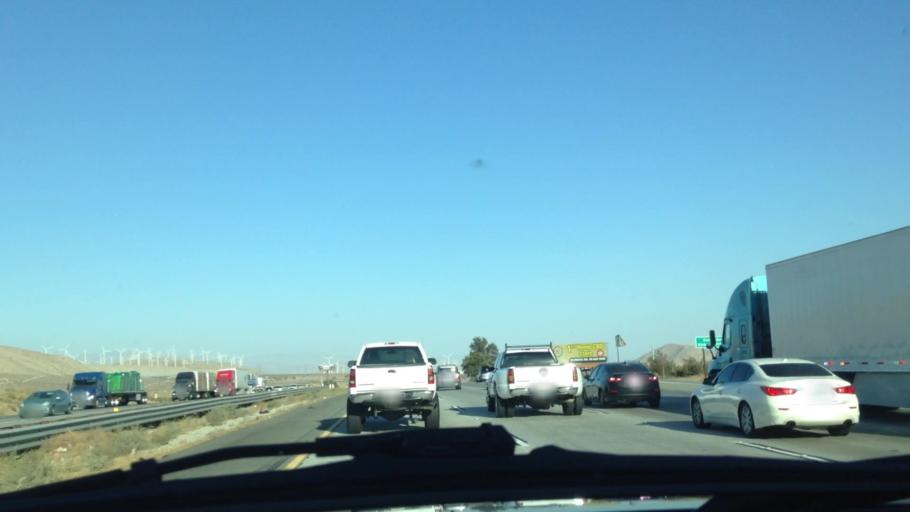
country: US
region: California
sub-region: Riverside County
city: Cabazon
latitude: 33.9227
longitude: -116.6848
